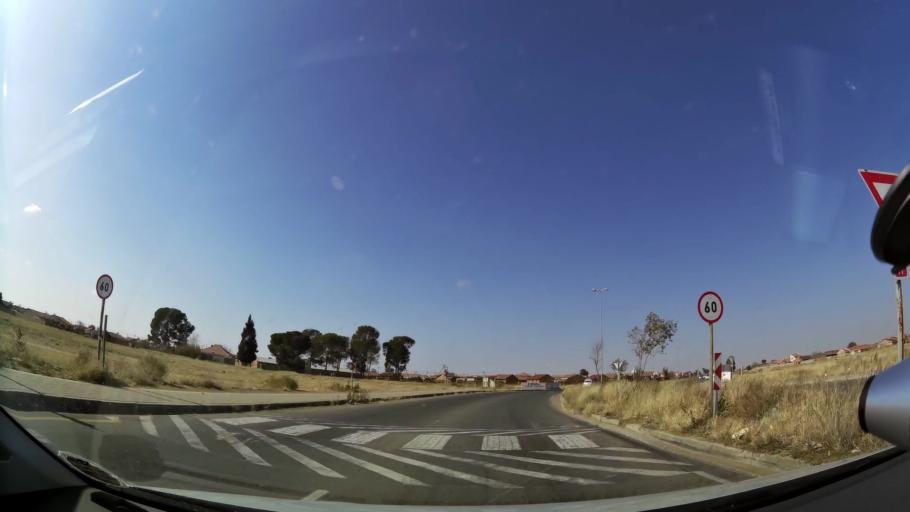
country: ZA
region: Orange Free State
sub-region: Mangaung Metropolitan Municipality
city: Bloemfontein
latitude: -29.1472
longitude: 26.2665
